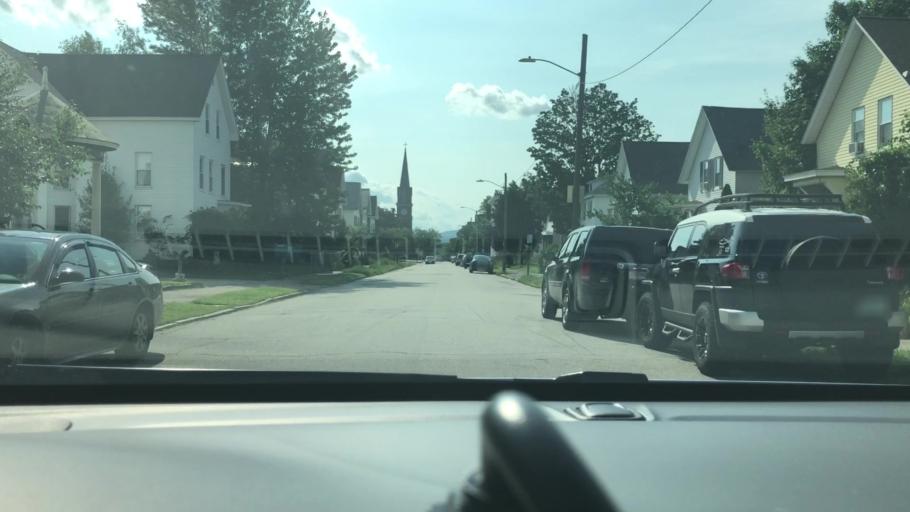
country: US
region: New Hampshire
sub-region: Hillsborough County
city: Manchester
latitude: 42.9894
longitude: -71.4535
